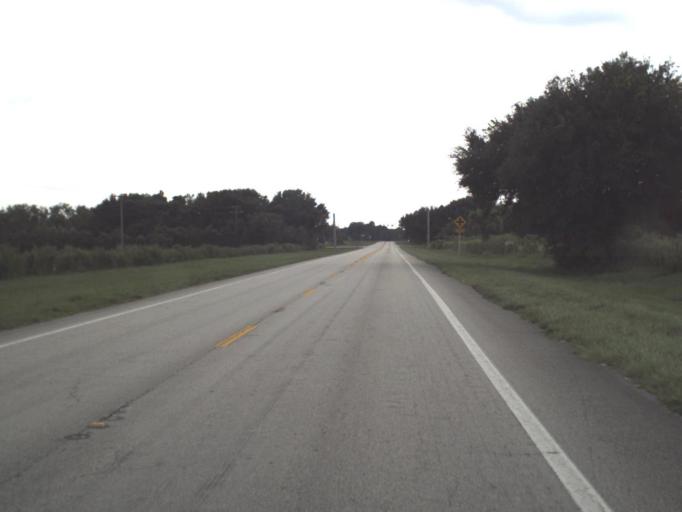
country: US
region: Florida
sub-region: Okeechobee County
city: Cypress Quarters
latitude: 27.3786
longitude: -80.8172
